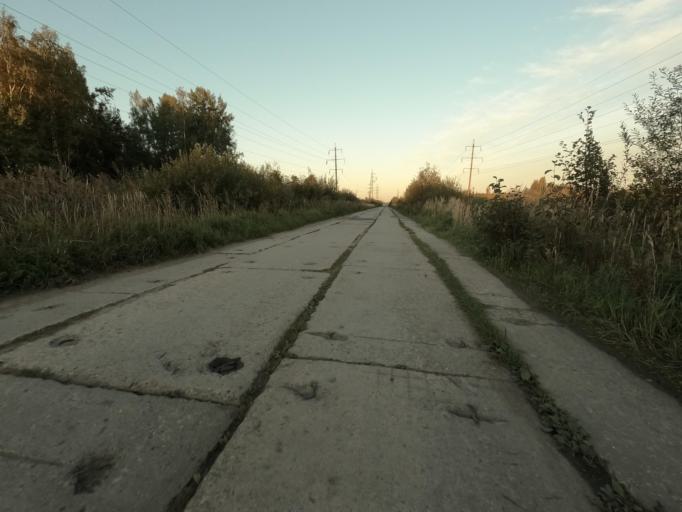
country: RU
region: Leningrad
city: Otradnoye
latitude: 59.7591
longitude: 30.7812
